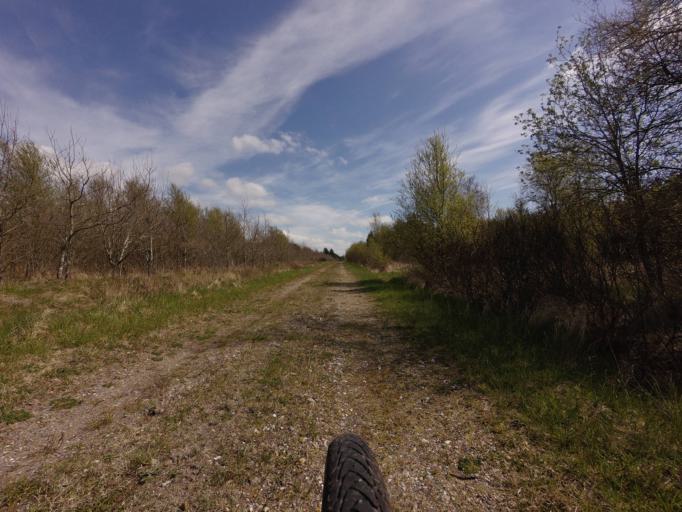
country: DK
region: North Denmark
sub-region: Jammerbugt Kommune
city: Brovst
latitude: 57.1695
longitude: 9.5605
